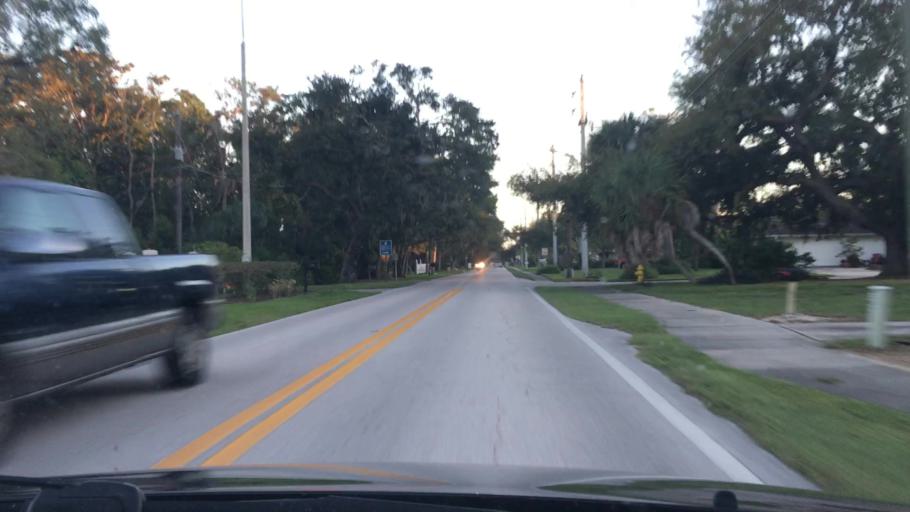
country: US
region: Florida
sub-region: Volusia County
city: Ormond Beach
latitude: 29.3083
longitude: -81.0669
